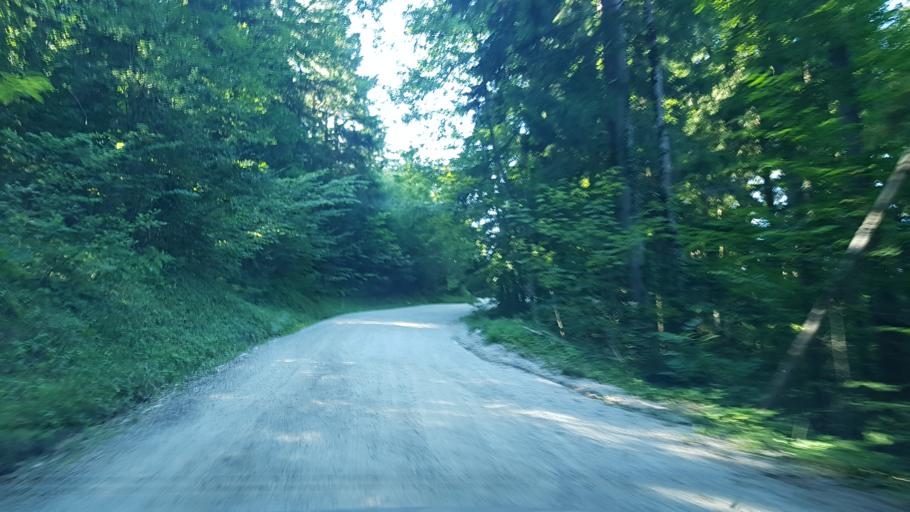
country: SI
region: Ravne na Koroskem
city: Kotlje
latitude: 46.5074
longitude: 14.9547
